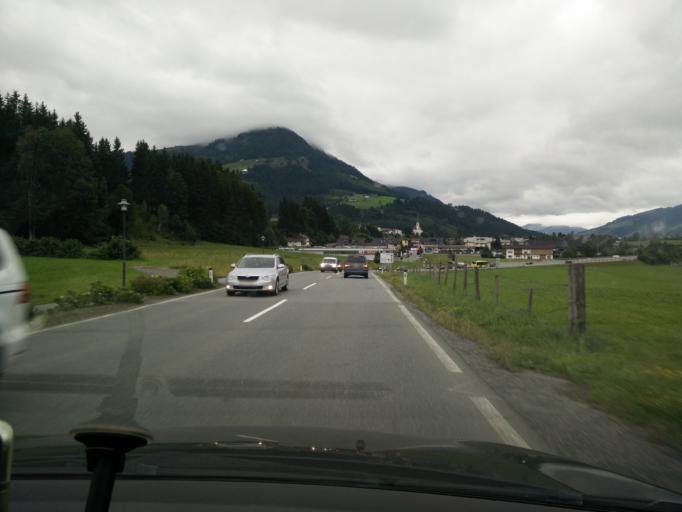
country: AT
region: Tyrol
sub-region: Politischer Bezirk Kitzbuhel
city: Kirchberg in Tirol
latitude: 47.4504
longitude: 12.3313
